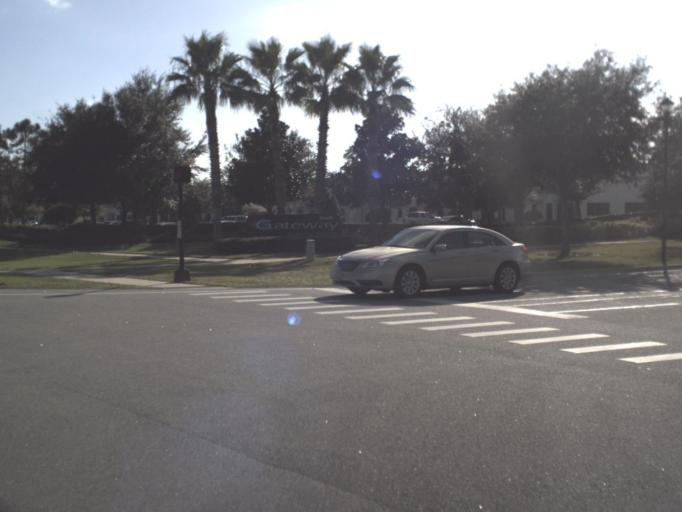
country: US
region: Florida
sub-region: Volusia County
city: Holly Hill
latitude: 29.2142
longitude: -81.0908
